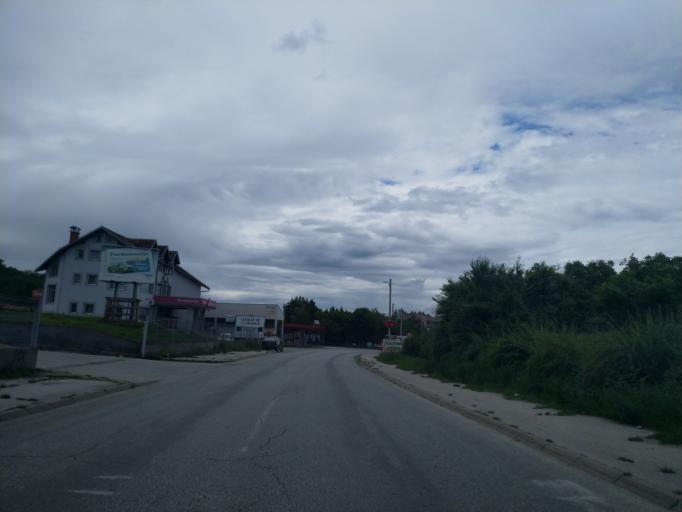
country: RS
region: Central Serbia
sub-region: Pomoravski Okrug
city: Jagodina
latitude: 43.9650
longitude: 21.2783
